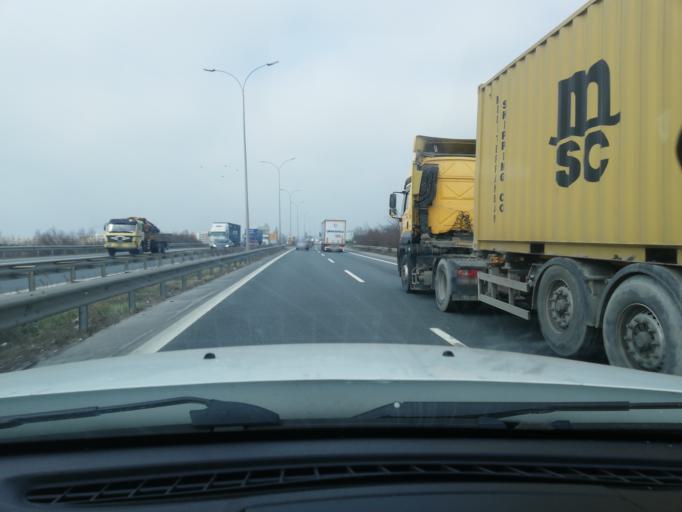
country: TR
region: Istanbul
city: Selimpasa
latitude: 41.0739
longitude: 28.3782
